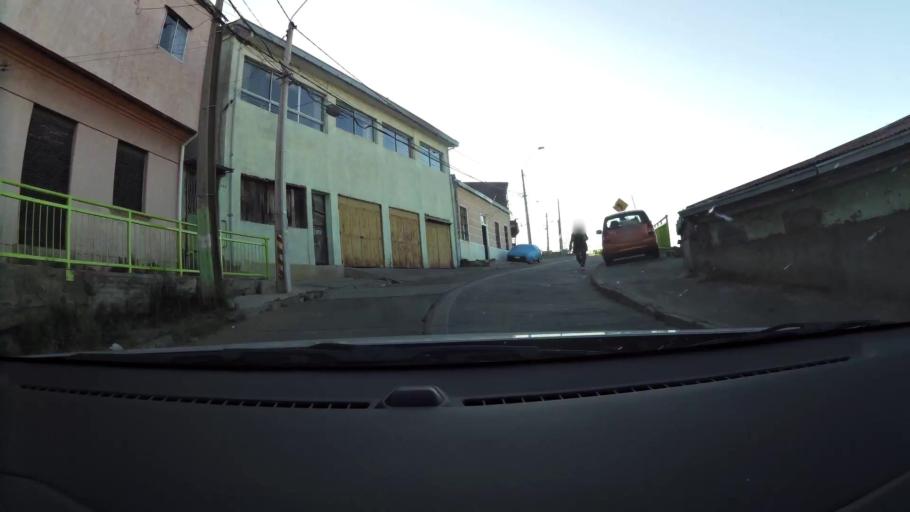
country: CL
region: Valparaiso
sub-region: Provincia de Valparaiso
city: Valparaiso
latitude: -33.0561
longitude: -71.6052
